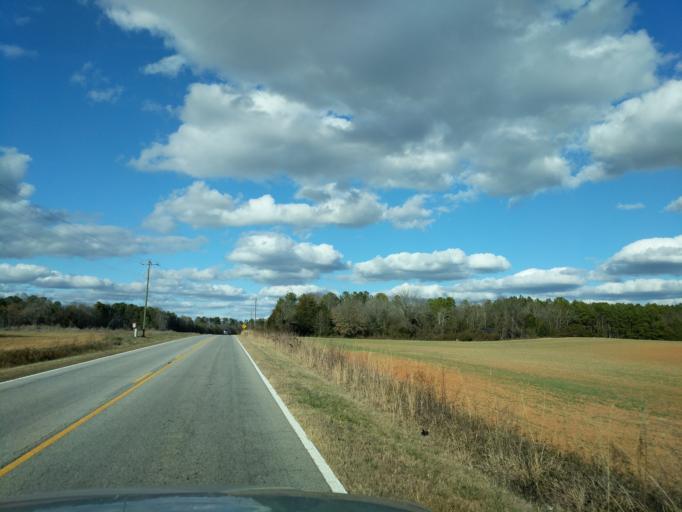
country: US
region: South Carolina
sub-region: Laurens County
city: Laurens
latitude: 34.4060
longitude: -82.0517
